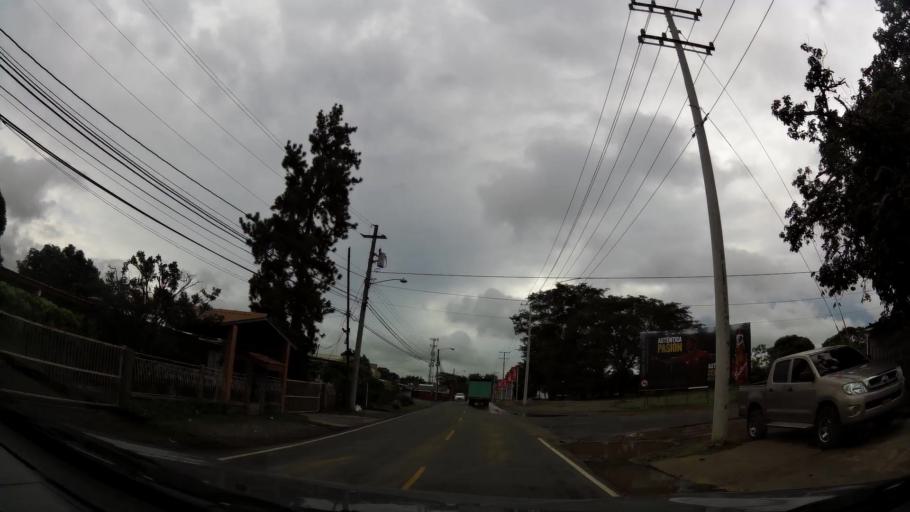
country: PA
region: Chiriqui
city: David
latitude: 8.4365
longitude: -82.4215
